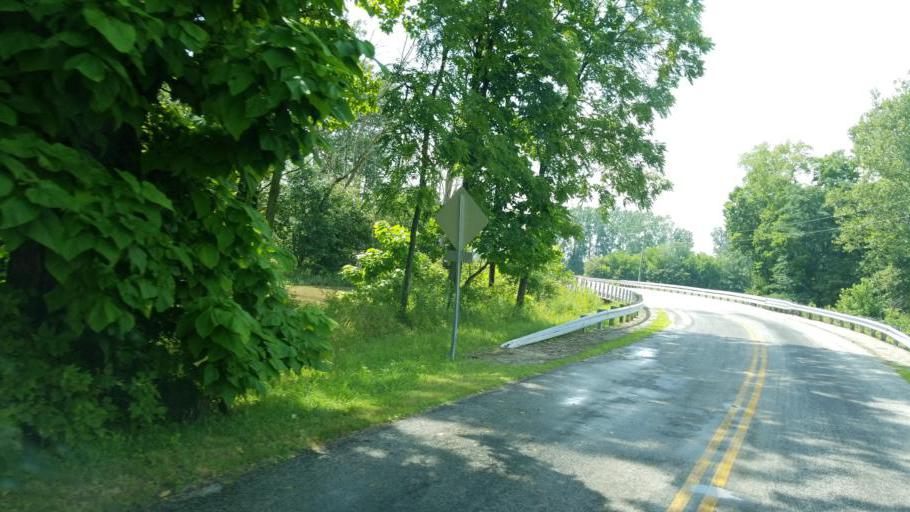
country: US
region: Ohio
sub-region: Union County
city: Richwood
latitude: 40.5591
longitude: -83.3317
